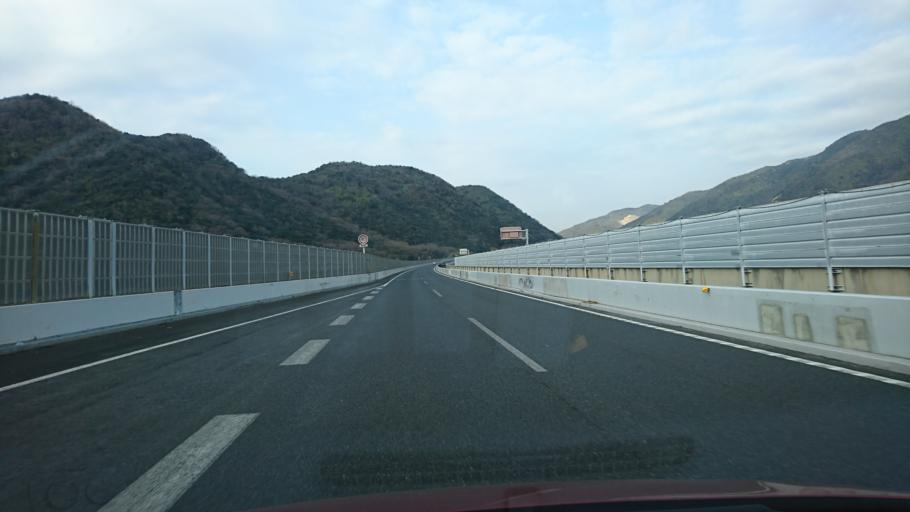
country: JP
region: Hyogo
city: Kariya
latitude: 34.7735
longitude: 134.3707
